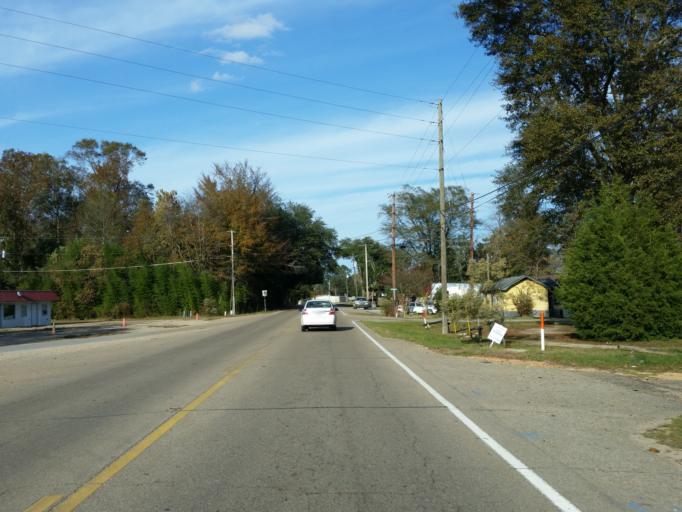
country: US
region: Mississippi
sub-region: Jones County
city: Ellisville
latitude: 31.6429
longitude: -89.1782
